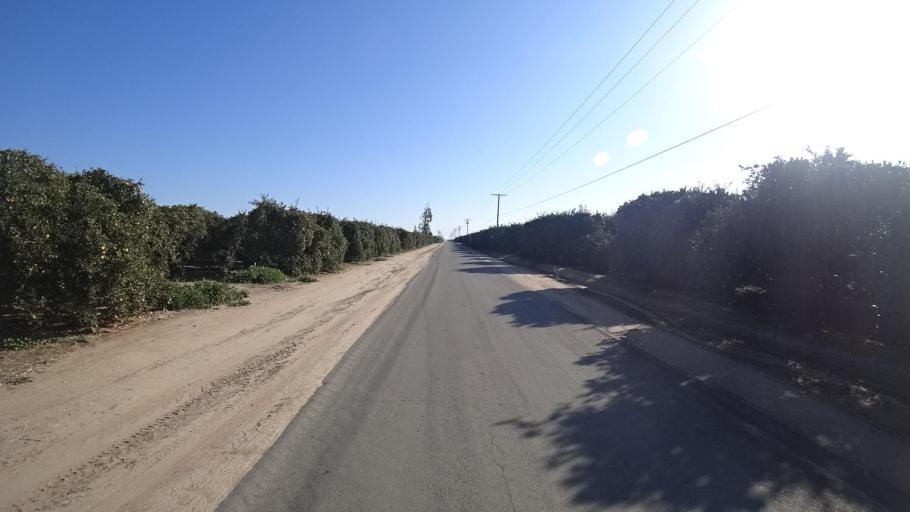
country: US
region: California
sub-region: Tulare County
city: Richgrove
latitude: 35.7325
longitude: -119.1378
